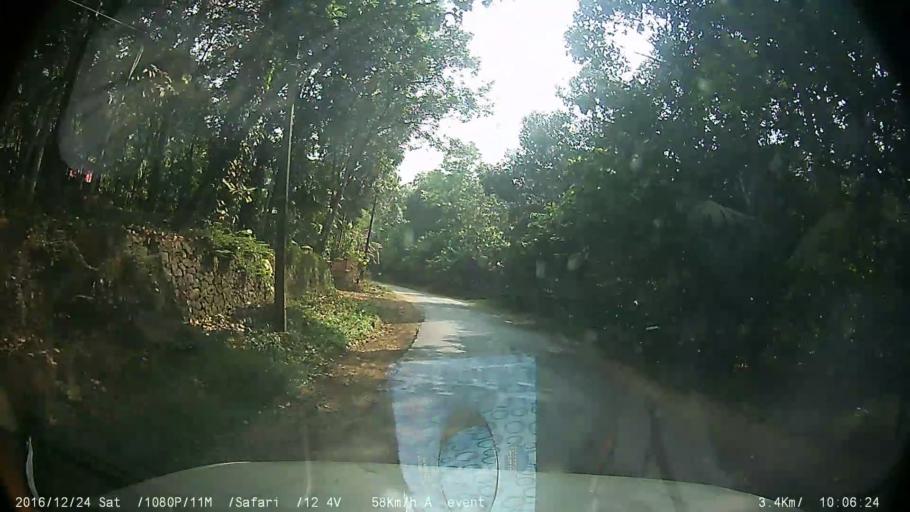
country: IN
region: Kerala
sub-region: Kottayam
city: Palackattumala
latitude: 9.7821
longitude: 76.5849
